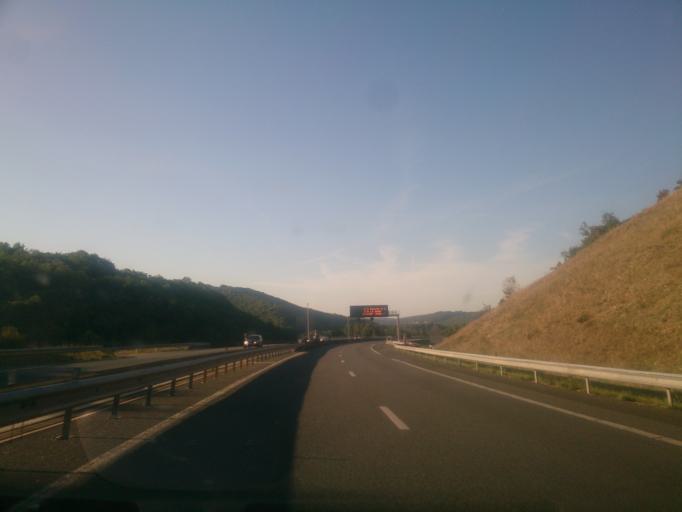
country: FR
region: Midi-Pyrenees
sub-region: Departement du Lot
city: Souillac
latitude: 44.8427
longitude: 1.4915
